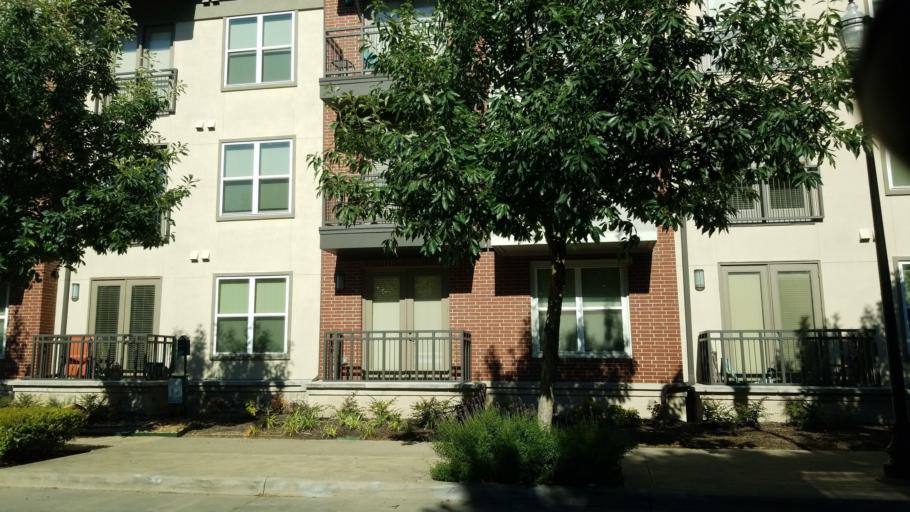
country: US
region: Texas
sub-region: Dallas County
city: Carrollton
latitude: 32.9519
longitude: -96.9047
